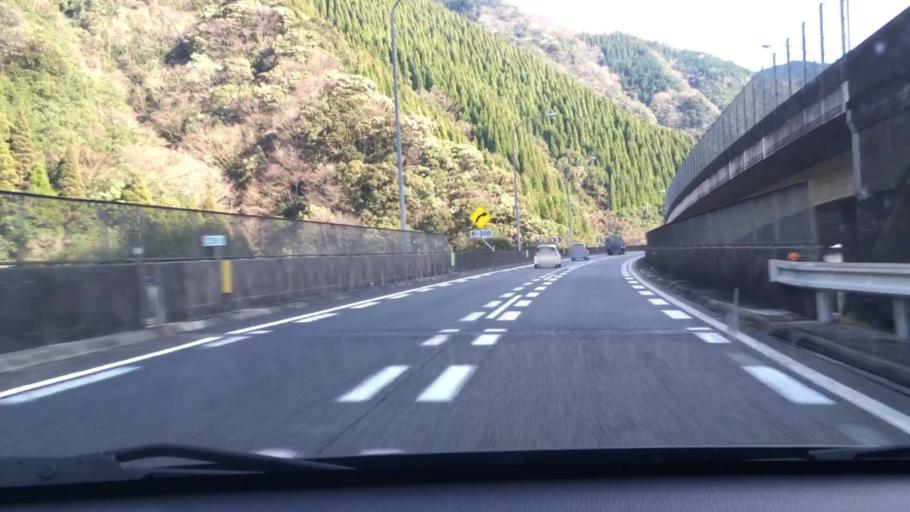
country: JP
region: Kumamoto
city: Hitoyoshi
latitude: 32.3270
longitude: 130.7552
